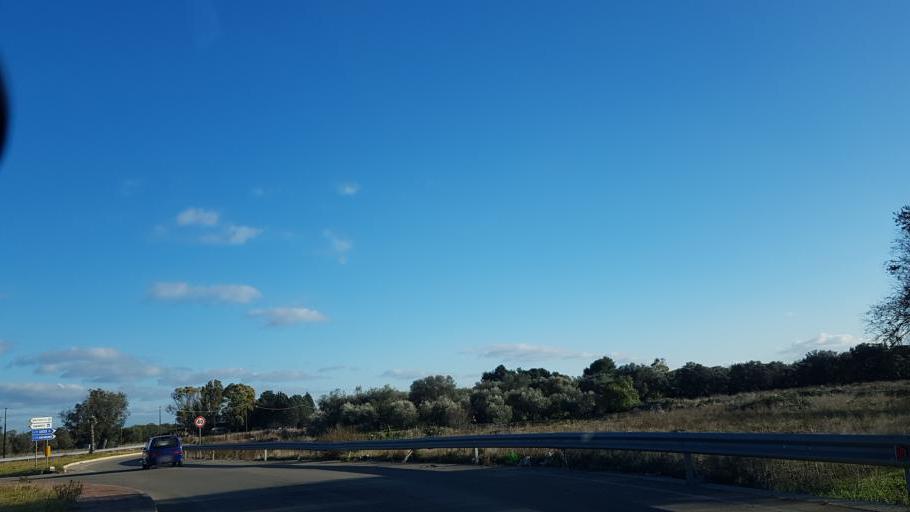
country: IT
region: Apulia
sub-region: Provincia di Brindisi
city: San Pietro Vernotico
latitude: 40.4765
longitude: 18.0075
